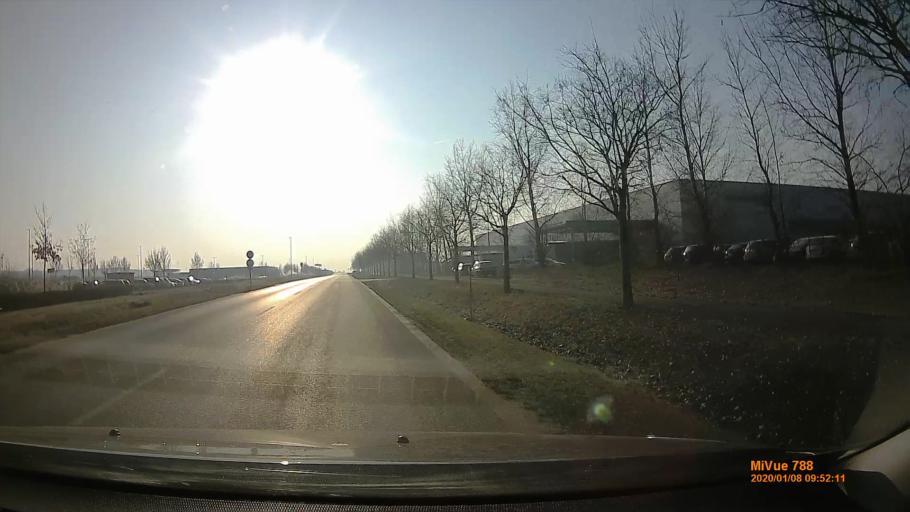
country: HU
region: Bacs-Kiskun
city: Kecskemet
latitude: 46.8697
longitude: 19.7031
